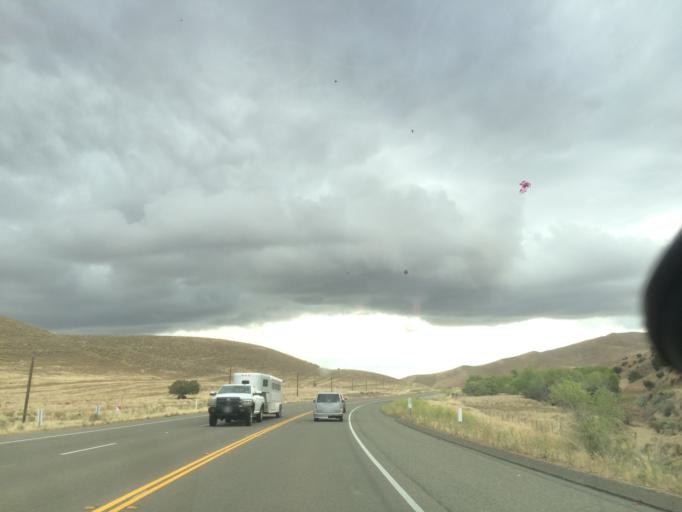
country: US
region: California
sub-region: Kings County
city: Avenal
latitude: 35.7749
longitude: -120.1526
